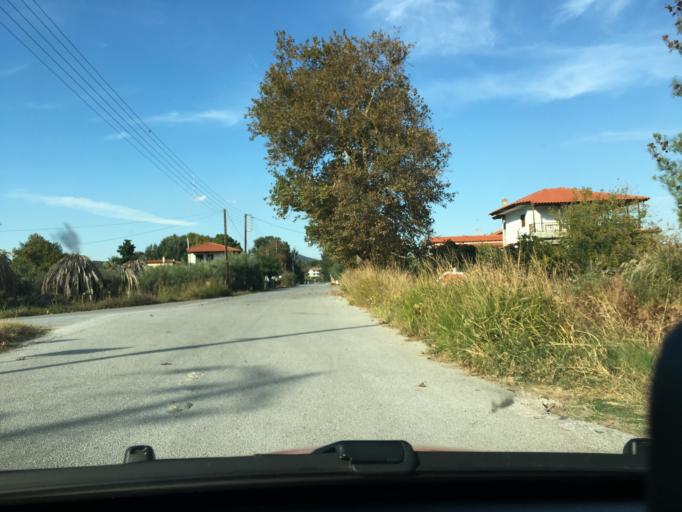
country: GR
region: Central Macedonia
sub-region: Nomos Chalkidikis
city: Agios Nikolaos
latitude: 40.2935
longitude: 23.6938
